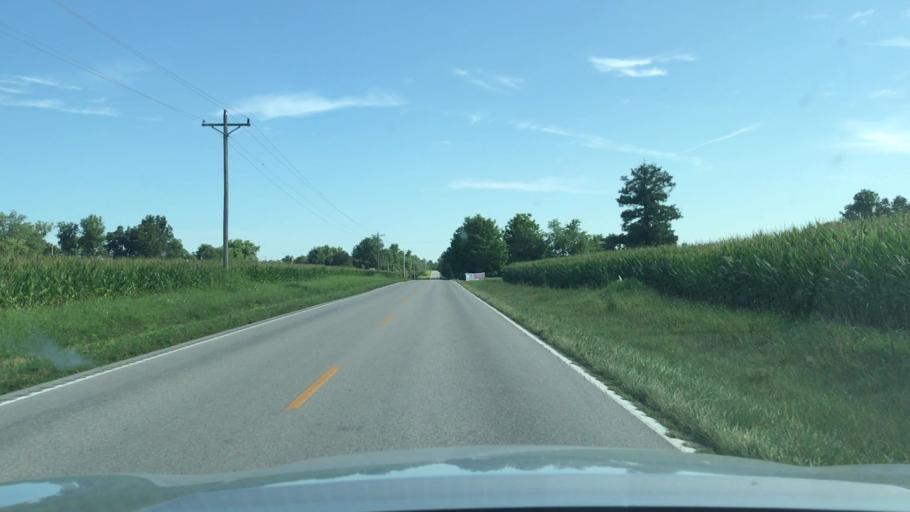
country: US
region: Kentucky
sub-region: Todd County
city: Elkton
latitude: 36.9215
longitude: -87.1627
